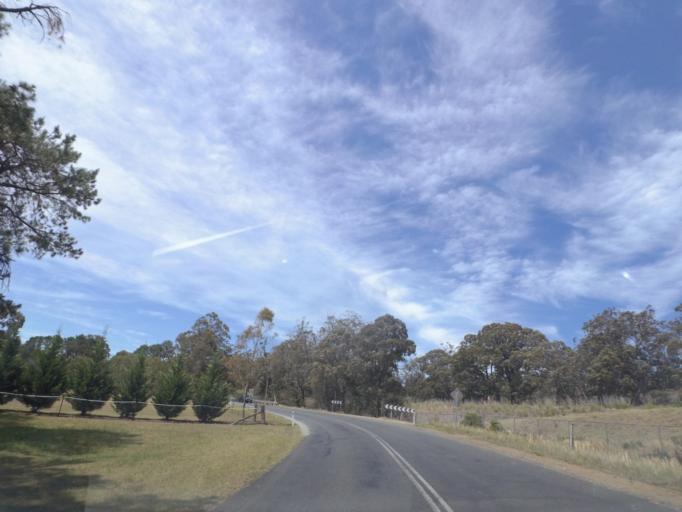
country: AU
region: New South Wales
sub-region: Wingecarribee
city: Colo Vale
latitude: -34.3760
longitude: 150.5380
